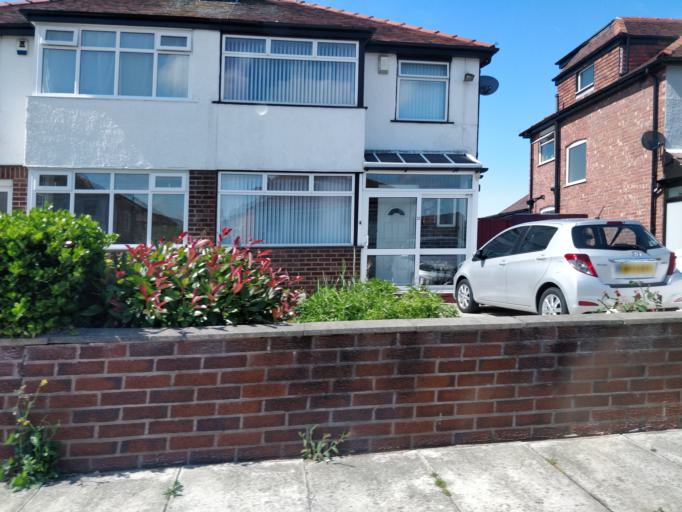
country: GB
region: England
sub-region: Lancashire
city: Banks
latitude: 53.6651
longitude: -2.9545
